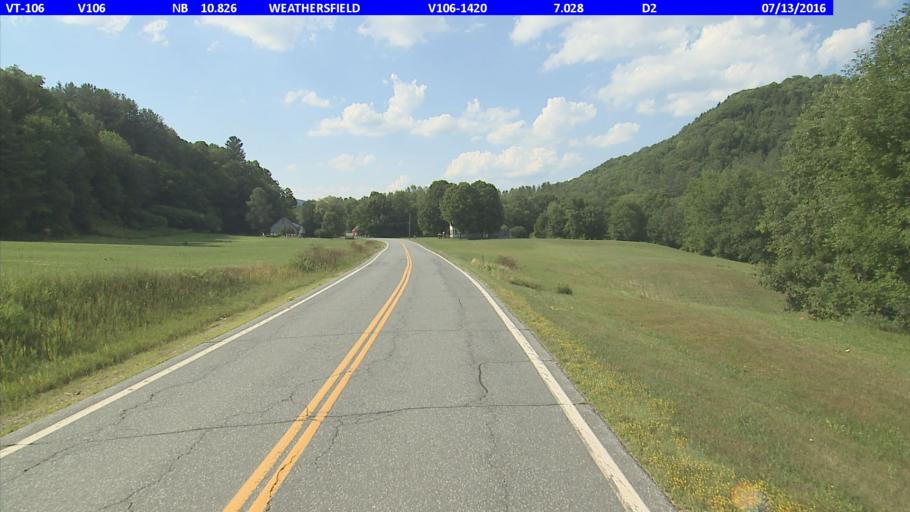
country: US
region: Vermont
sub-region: Windsor County
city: Springfield
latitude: 43.4360
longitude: -72.5292
